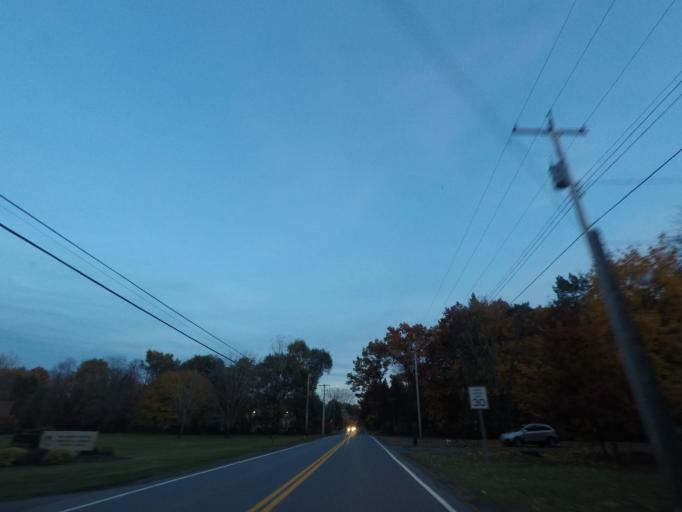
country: US
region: New York
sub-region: Schenectady County
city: Rotterdam
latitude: 42.7514
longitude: -73.9181
